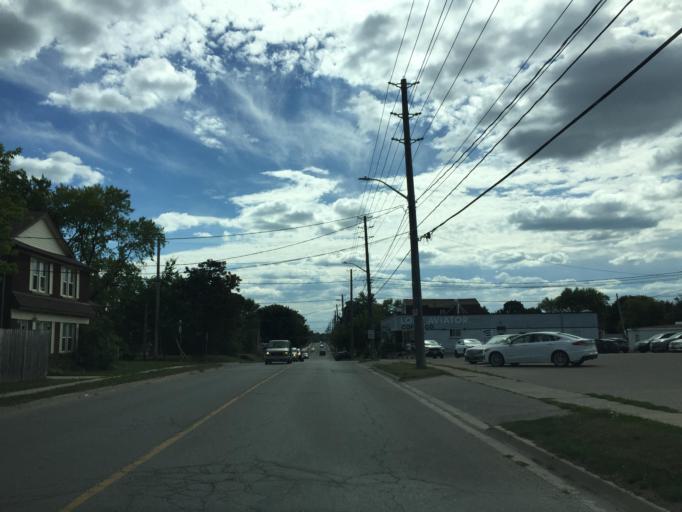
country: CA
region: Ontario
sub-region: Wellington County
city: Guelph
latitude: 43.5500
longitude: -80.2264
